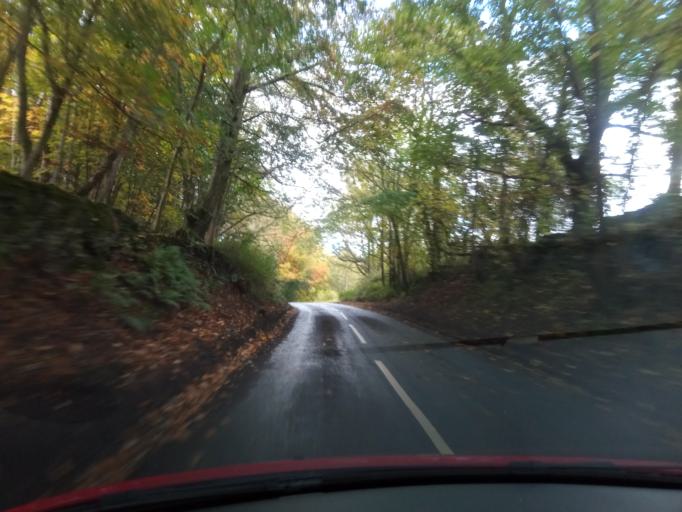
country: GB
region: Scotland
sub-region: The Scottish Borders
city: Newtown St Boswells
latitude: 55.5534
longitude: -2.7052
